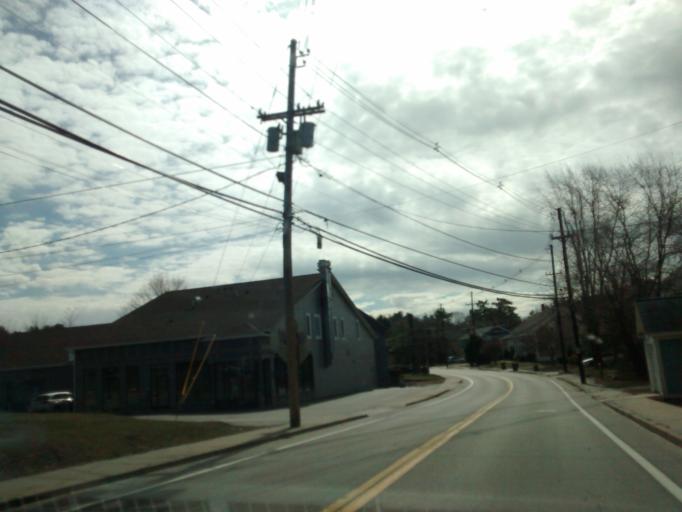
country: US
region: Rhode Island
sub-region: Providence County
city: Harrisville
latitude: 41.9641
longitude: -71.6757
